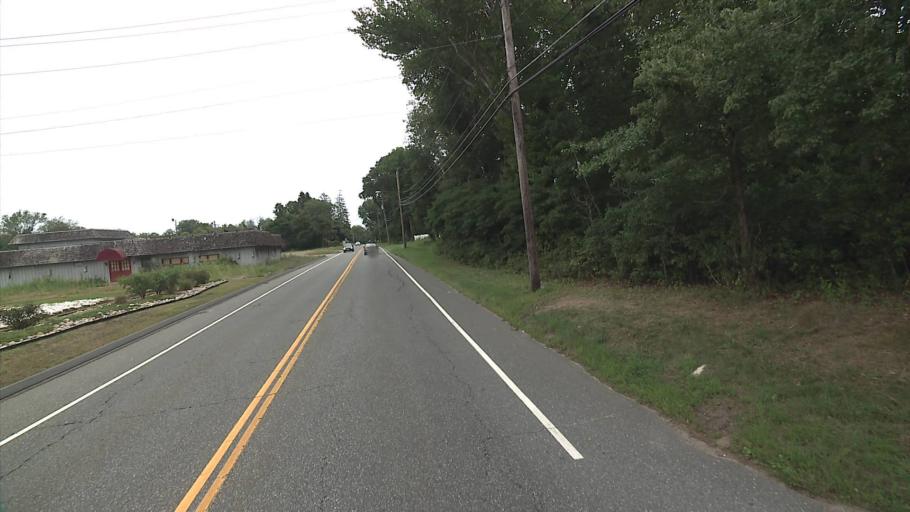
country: US
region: Connecticut
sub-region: Middlesex County
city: Old Saybrook Center
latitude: 41.2885
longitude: -72.2900
